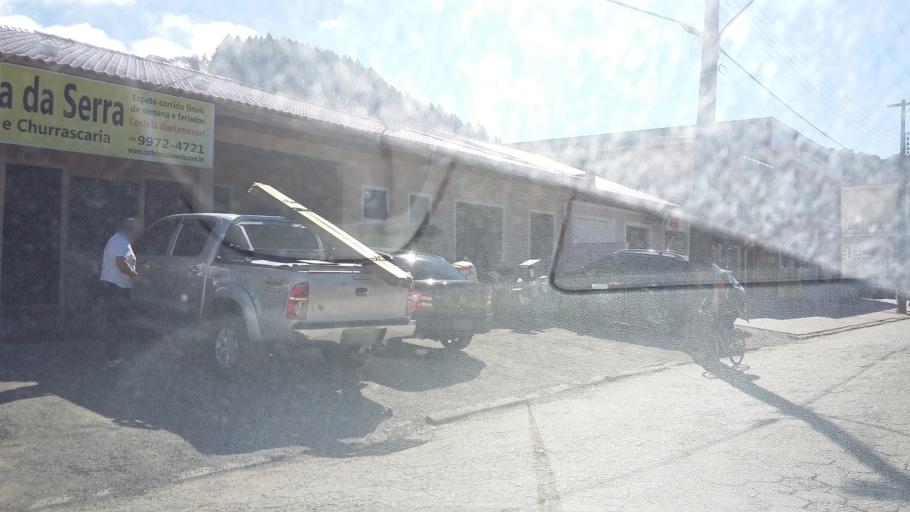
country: BR
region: Santa Catarina
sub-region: Santo Amaro Da Imperatriz
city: Santo Amaro da Imperatriz
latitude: -27.6731
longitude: -49.0132
